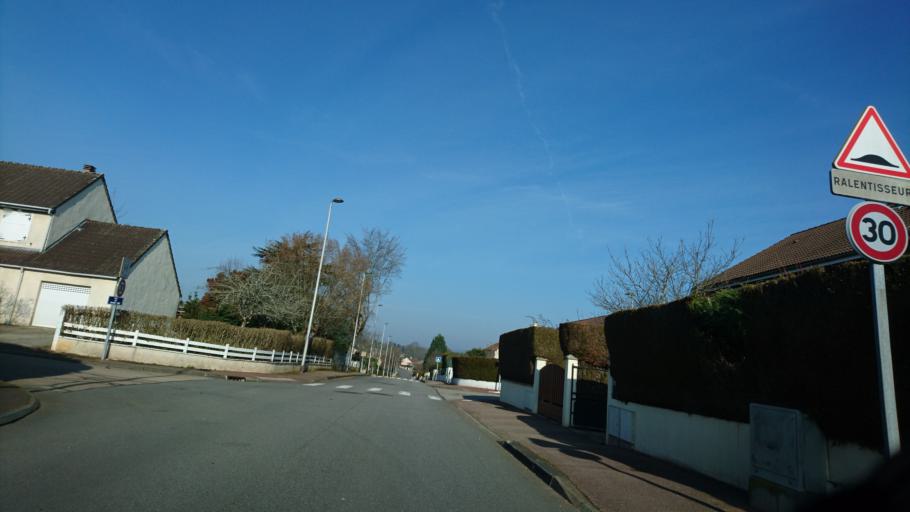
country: FR
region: Limousin
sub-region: Departement de la Haute-Vienne
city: Le Palais-sur-Vienne
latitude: 45.8784
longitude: 1.3046
